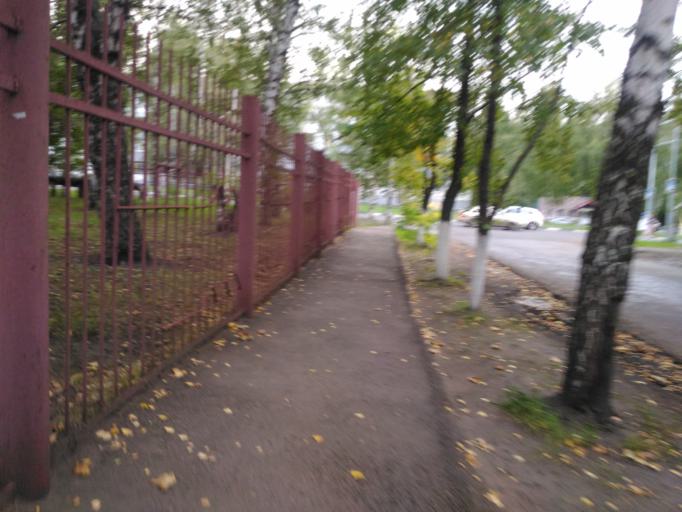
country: RU
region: Ulyanovsk
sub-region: Ulyanovskiy Rayon
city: Ulyanovsk
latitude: 54.2651
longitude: 48.3352
